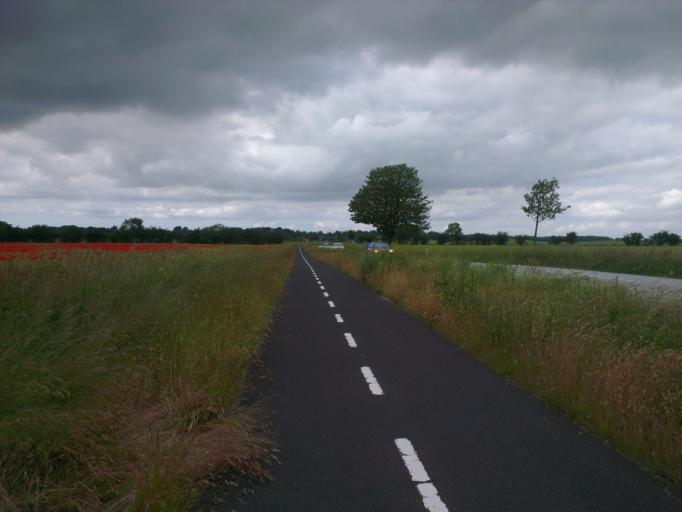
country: DK
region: Capital Region
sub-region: Frederikssund Kommune
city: Skibby
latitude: 55.6935
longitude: 11.9492
